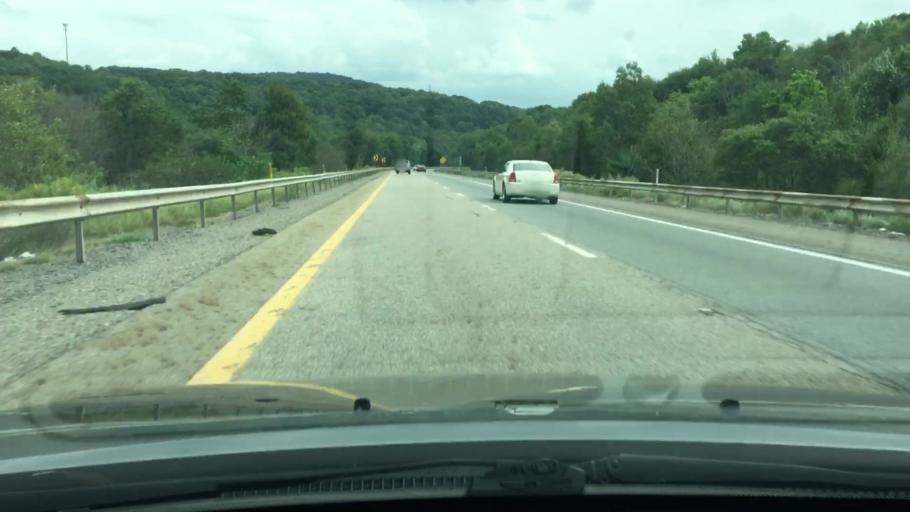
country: US
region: Pennsylvania
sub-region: Schuylkill County
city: Tremont
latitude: 40.6141
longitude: -76.4276
